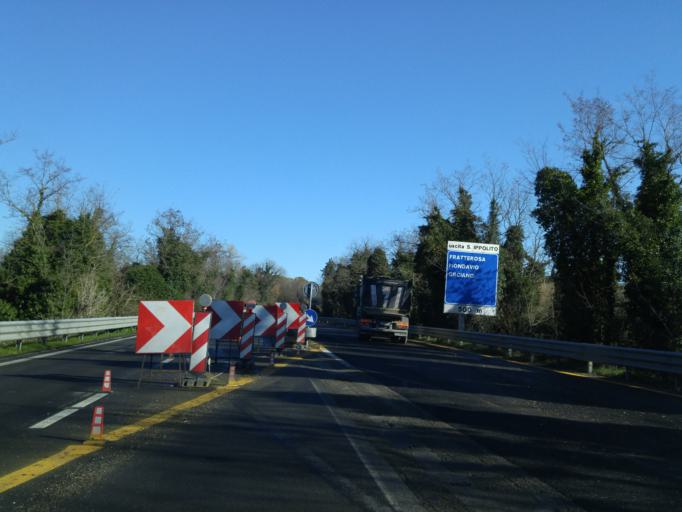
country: IT
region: The Marches
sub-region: Provincia di Pesaro e Urbino
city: Sant'Ippolito
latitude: 43.6990
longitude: 12.8642
